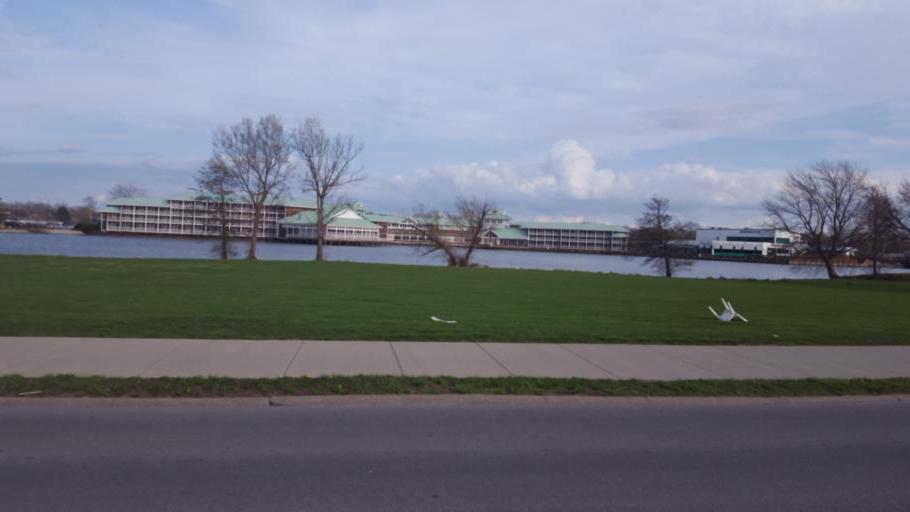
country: US
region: Ohio
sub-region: Erie County
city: Sandusky
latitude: 41.4441
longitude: -82.6800
